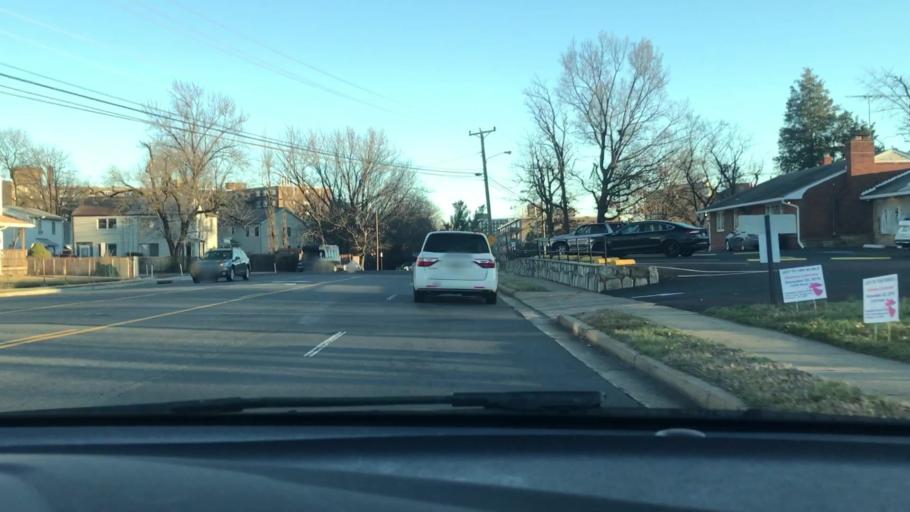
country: US
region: Virginia
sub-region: Fairfax County
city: Baileys Crossroads
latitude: 38.8553
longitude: -77.1234
